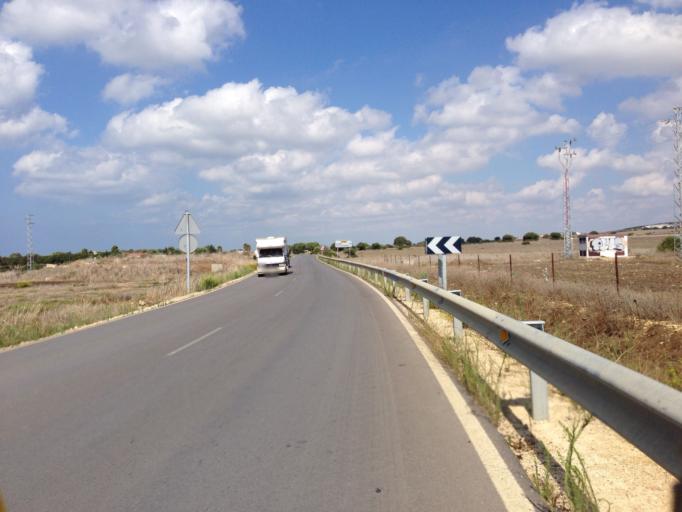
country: ES
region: Andalusia
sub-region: Provincia de Cadiz
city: Conil de la Frontera
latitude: 36.2229
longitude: -6.0423
